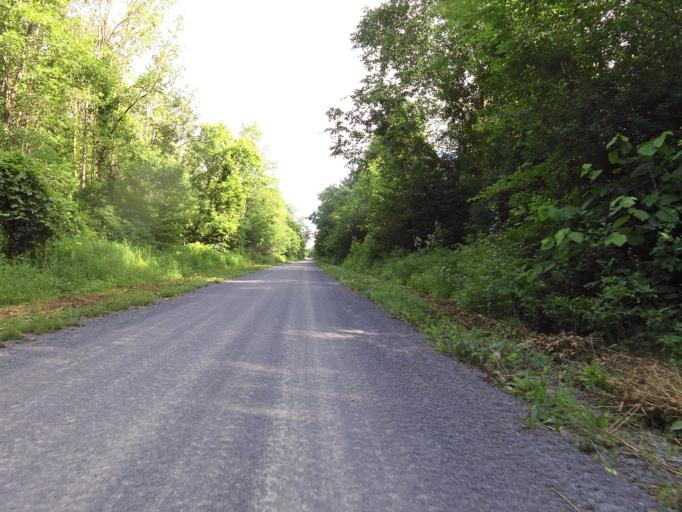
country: CA
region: Ontario
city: Arnprior
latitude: 45.3235
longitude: -76.2875
